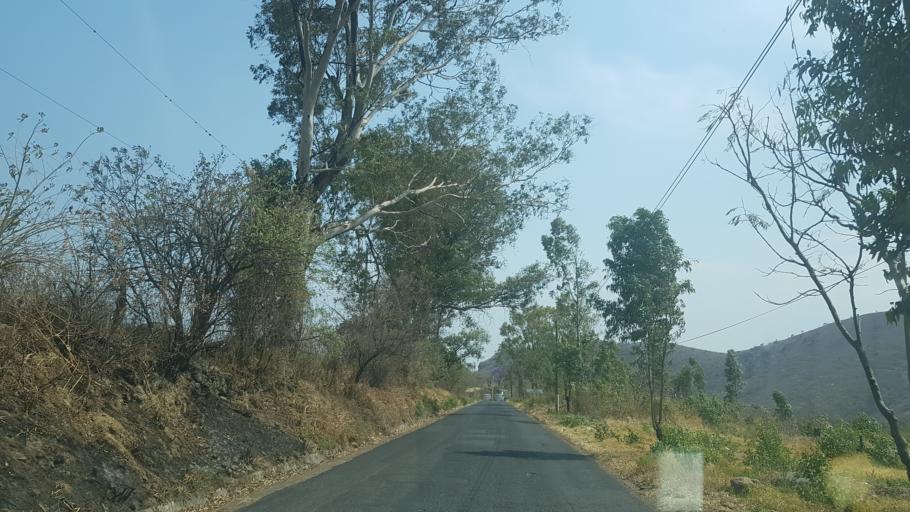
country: MX
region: Puebla
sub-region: Tianguismanalco
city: San Martin Tlapala
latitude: 18.9551
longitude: -98.4584
